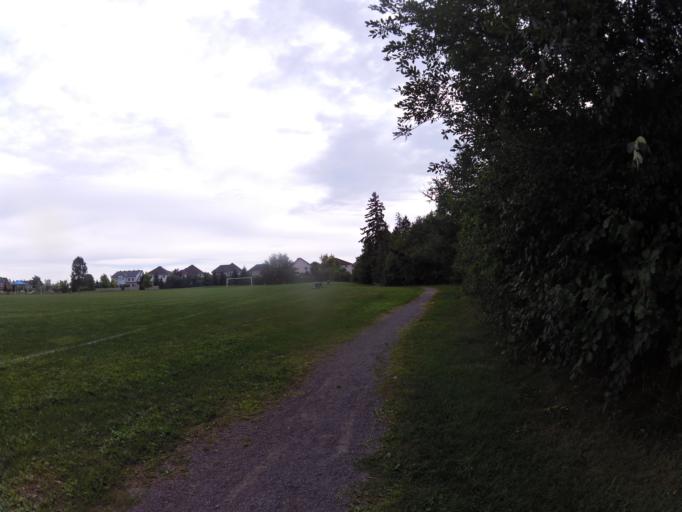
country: CA
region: Ontario
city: Bells Corners
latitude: 45.2776
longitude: -75.9337
